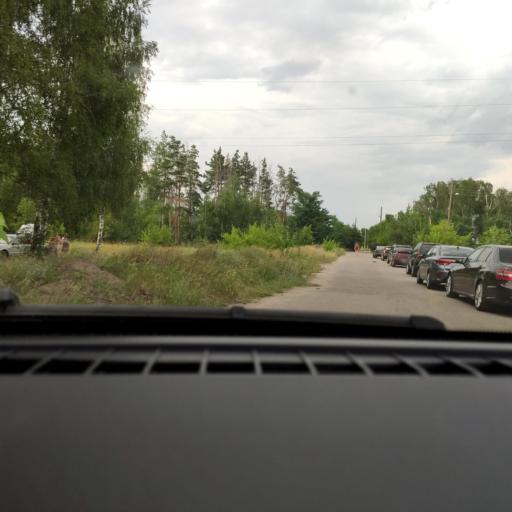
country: RU
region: Voronezj
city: Somovo
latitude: 51.7340
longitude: 39.3202
